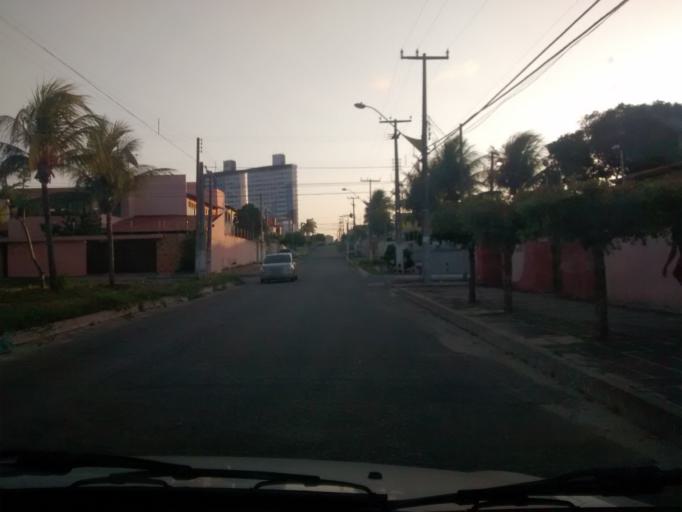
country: BR
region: Rio Grande do Norte
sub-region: Natal
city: Natal
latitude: -5.8688
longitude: -35.1881
